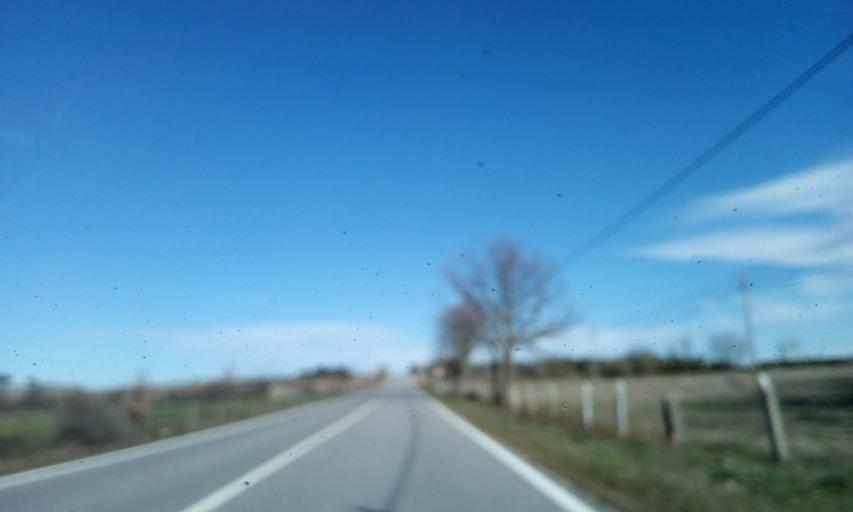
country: ES
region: Castille and Leon
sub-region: Provincia de Salamanca
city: Fuentes de Onoro
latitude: 40.6144
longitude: -6.8798
